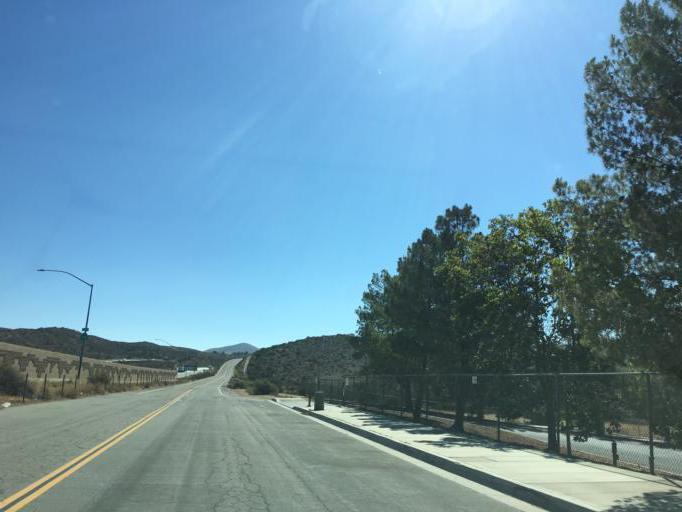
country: US
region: California
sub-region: Los Angeles County
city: Acton
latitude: 34.4918
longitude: -118.1945
